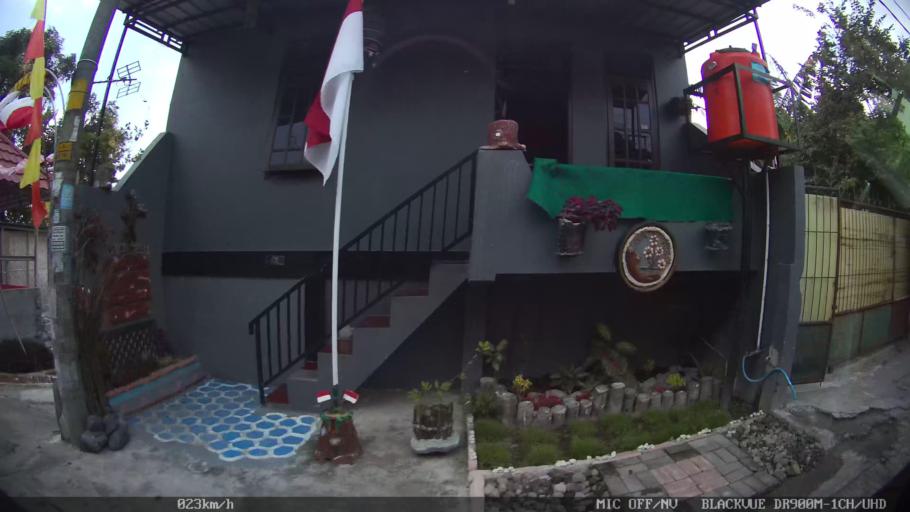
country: ID
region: Daerah Istimewa Yogyakarta
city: Yogyakarta
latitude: -7.8177
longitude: 110.4059
